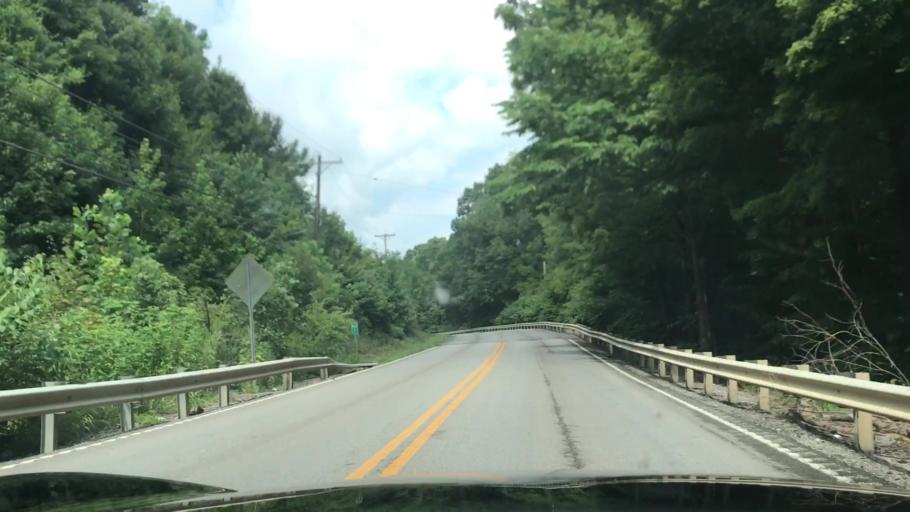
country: US
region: Kentucky
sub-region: Muhlenberg County
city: Central City
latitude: 37.2138
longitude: -87.0606
